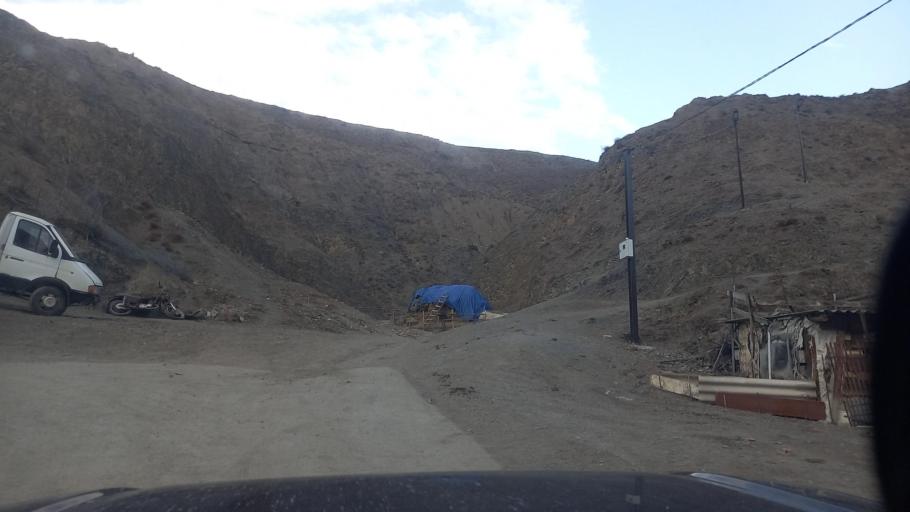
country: RU
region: Ingushetiya
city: Dzhayrakh
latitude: 42.8030
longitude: 44.7545
